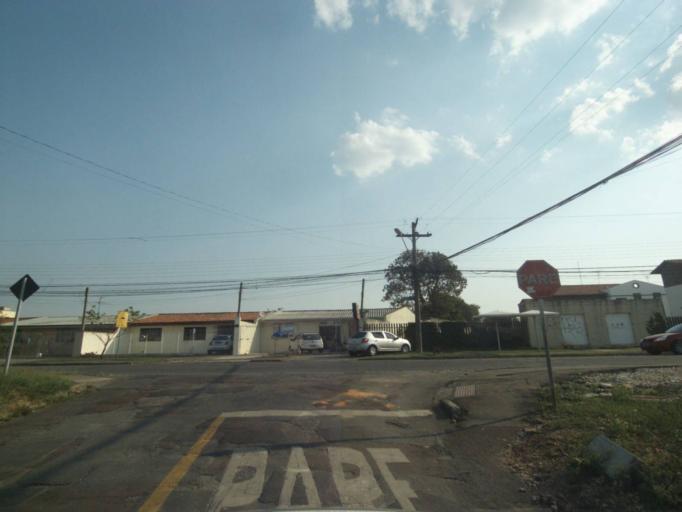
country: BR
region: Parana
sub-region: Sao Jose Dos Pinhais
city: Sao Jose dos Pinhais
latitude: -25.5332
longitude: -49.2387
